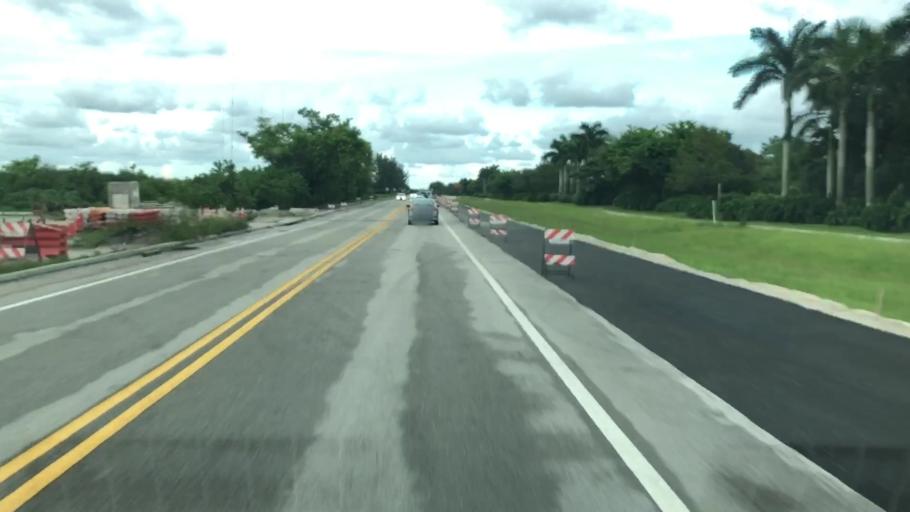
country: US
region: Florida
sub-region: Broward County
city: Parkland
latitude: 26.3344
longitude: -80.2719
